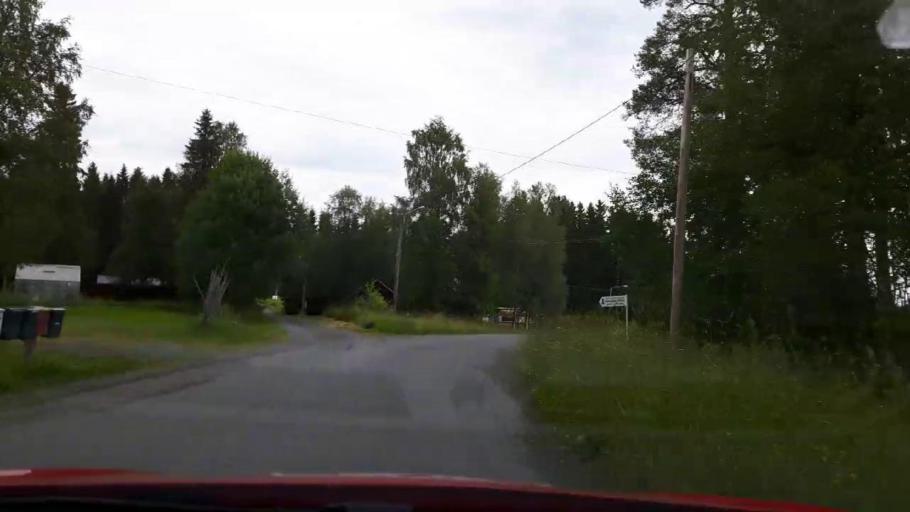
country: SE
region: Jaemtland
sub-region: OEstersunds Kommun
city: Lit
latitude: 63.3721
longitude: 15.1877
